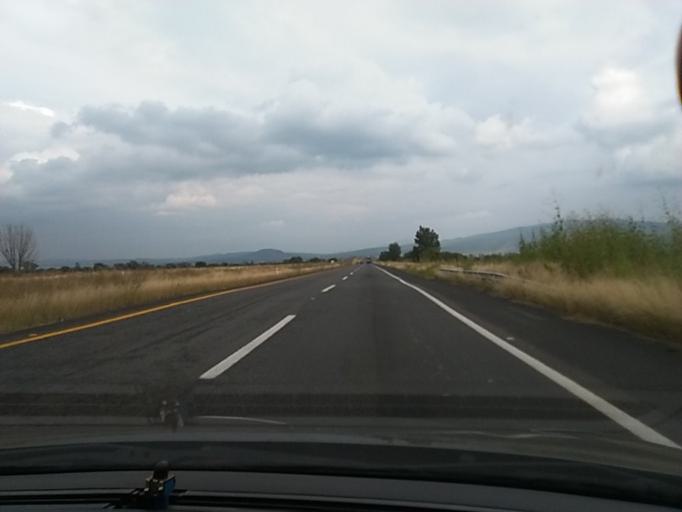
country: MX
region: Michoacan
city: Ecuandureo
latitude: 20.1772
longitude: -102.2520
